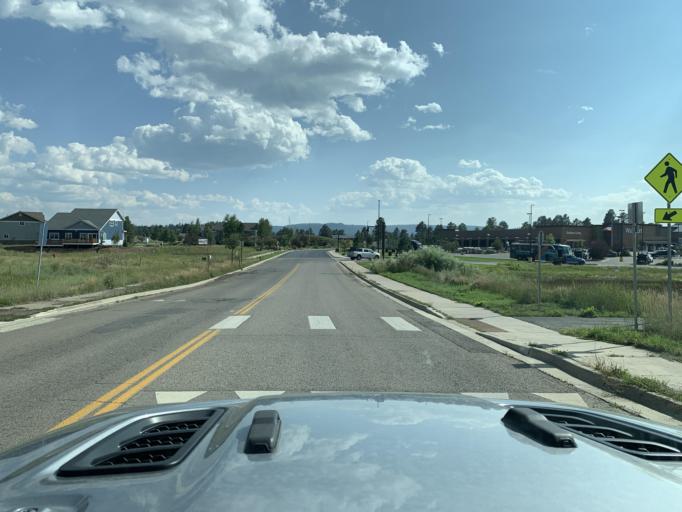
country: US
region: Colorado
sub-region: Archuleta County
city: Pagosa Springs
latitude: 37.2610
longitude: -107.0611
